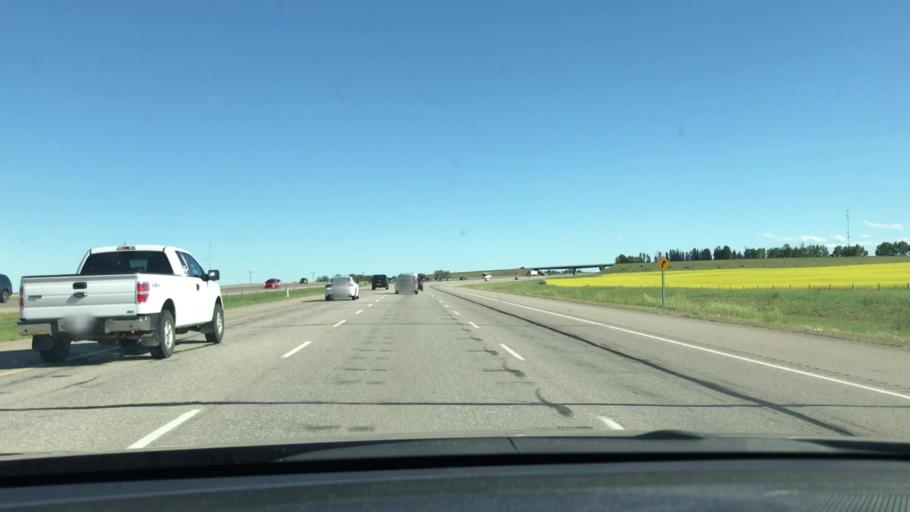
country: CA
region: Alberta
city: Crossfield
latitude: 51.4379
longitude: -114.0051
